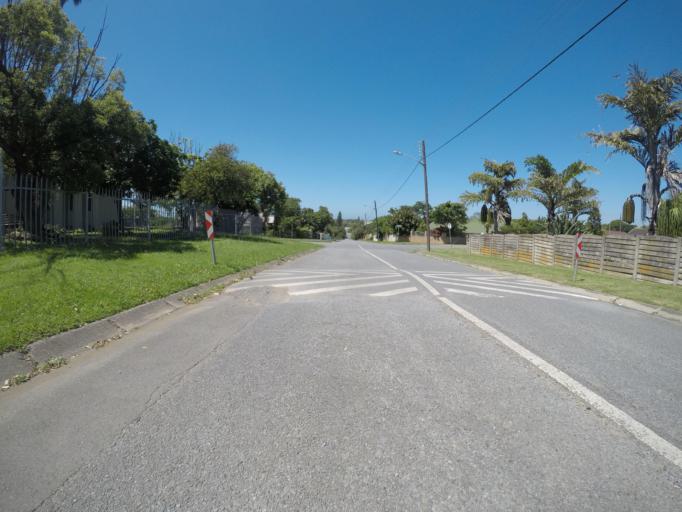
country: ZA
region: Eastern Cape
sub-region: Buffalo City Metropolitan Municipality
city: East London
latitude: -32.9688
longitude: 27.9426
